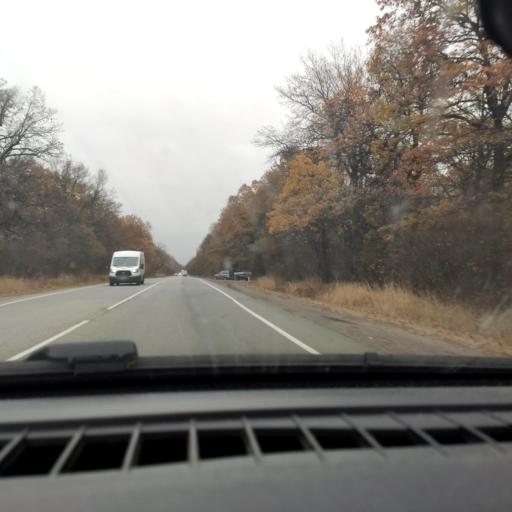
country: RU
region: Voronezj
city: Devitsa
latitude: 51.6156
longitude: 38.9832
